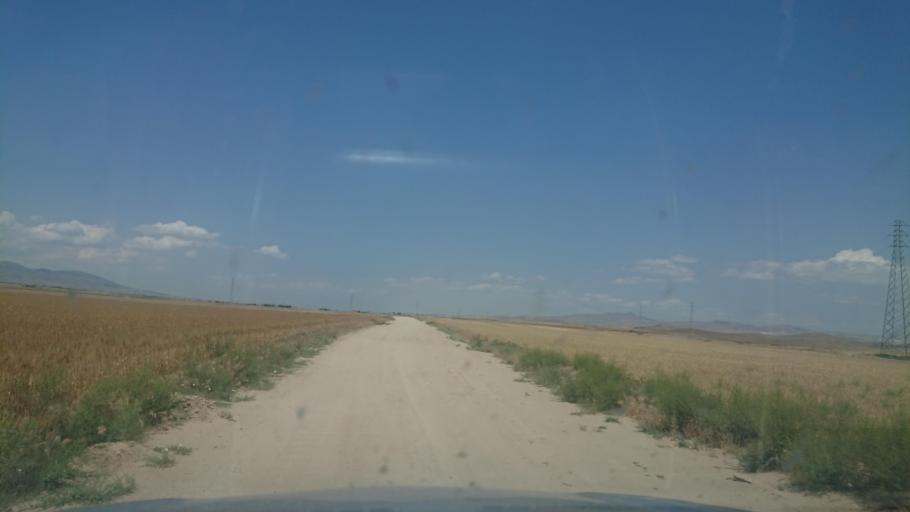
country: TR
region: Aksaray
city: Sariyahsi
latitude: 39.0024
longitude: 33.8885
